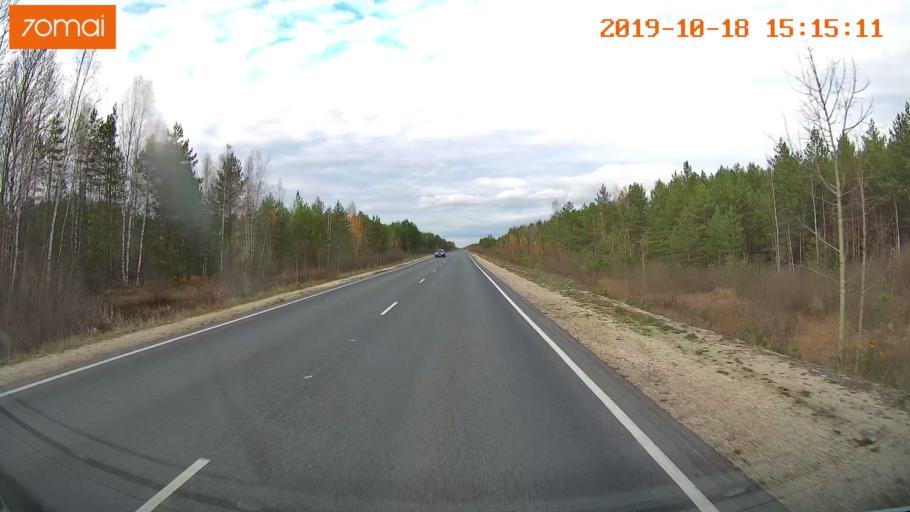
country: RU
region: Vladimir
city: Gus'-Khrustal'nyy
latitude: 55.6149
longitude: 40.7221
